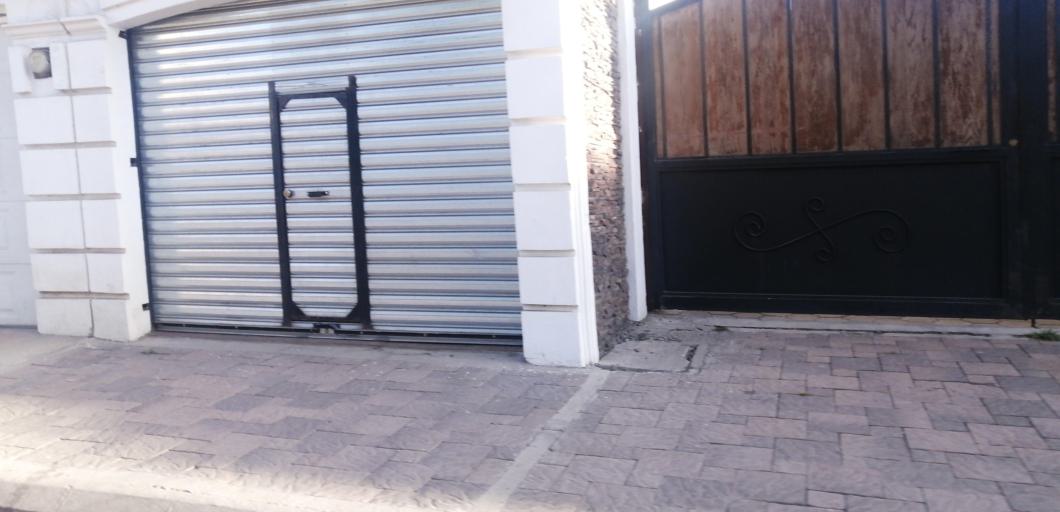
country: GT
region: Quetzaltenango
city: Olintepeque
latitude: 14.8666
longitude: -91.5217
